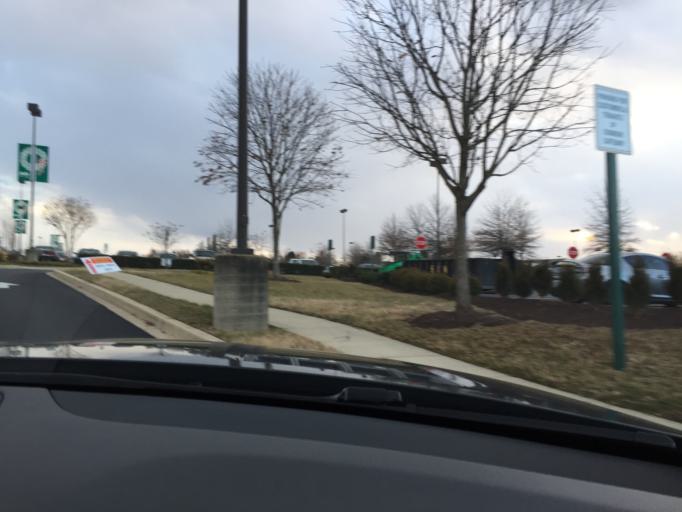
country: US
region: Maryland
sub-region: Calvert County
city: Dunkirk
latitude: 38.7254
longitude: -76.6576
